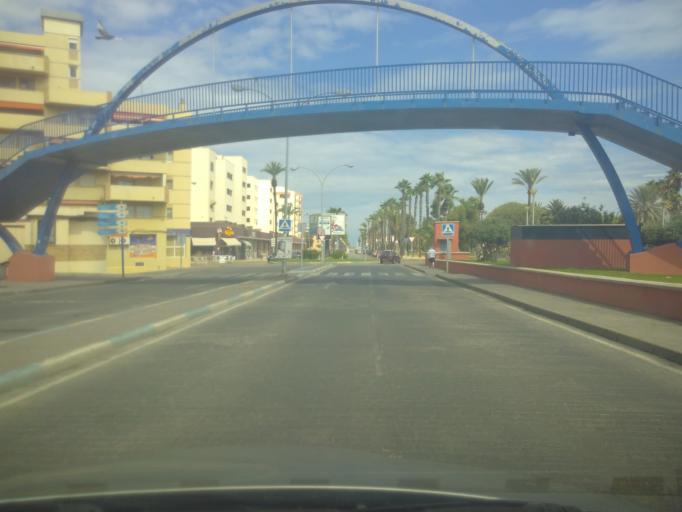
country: ES
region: Andalusia
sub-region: Provincia de Cadiz
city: La Linea de la Concepcion
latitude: 36.1598
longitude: -5.3481
